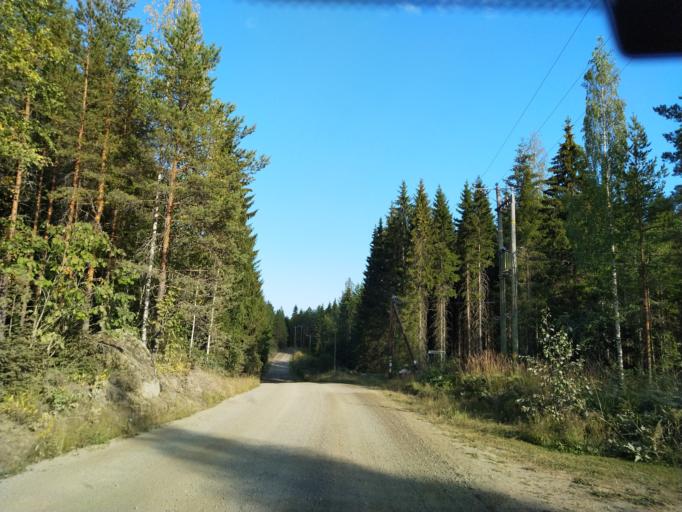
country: FI
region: Central Finland
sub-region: Jaemsae
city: Kuhmoinen
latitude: 61.6909
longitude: 24.9540
